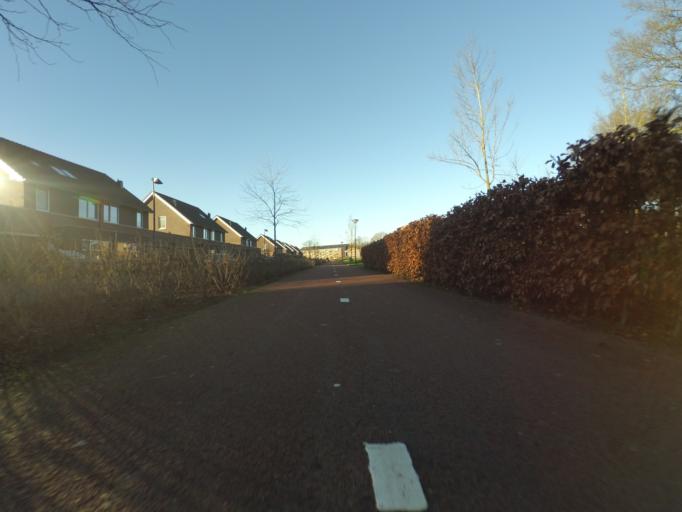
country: NL
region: Gelderland
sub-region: Gemeente Putten
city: Putten
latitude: 52.2603
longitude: 5.5857
